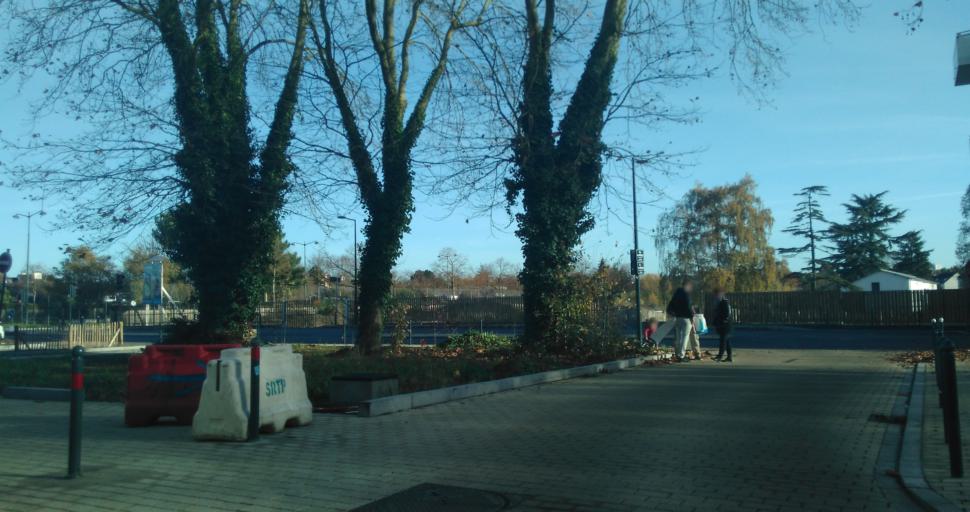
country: FR
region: Brittany
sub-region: Departement d'Ille-et-Vilaine
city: Rennes
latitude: 48.1300
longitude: -1.6765
